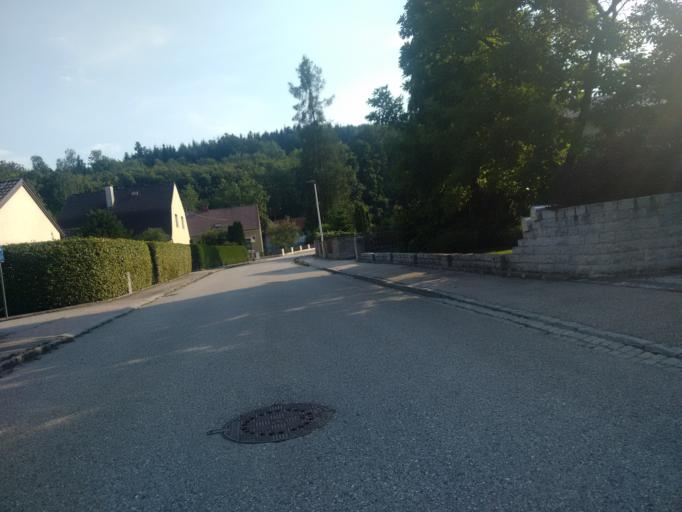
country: AT
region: Upper Austria
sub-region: Politischer Bezirk Grieskirchen
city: Bad Schallerbach
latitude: 48.2256
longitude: 13.9302
